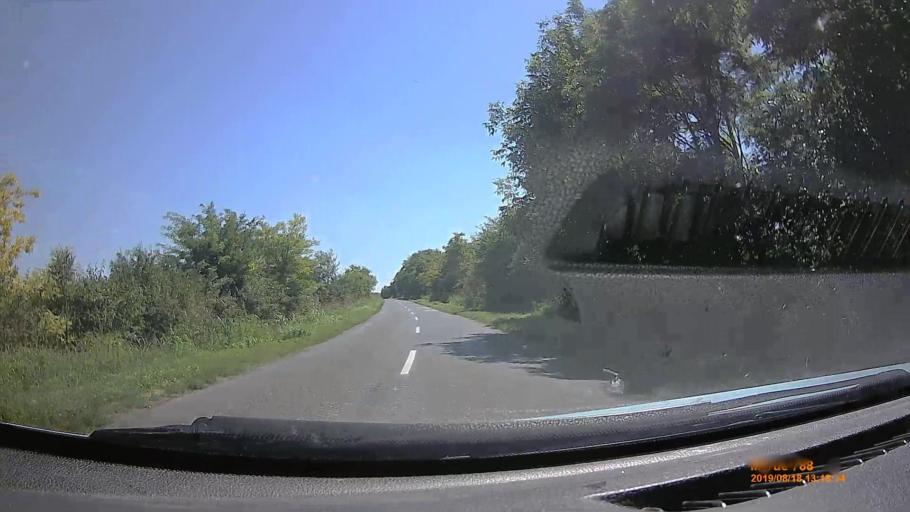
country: HU
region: Fejer
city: Sarbogard
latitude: 46.8417
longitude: 18.5611
